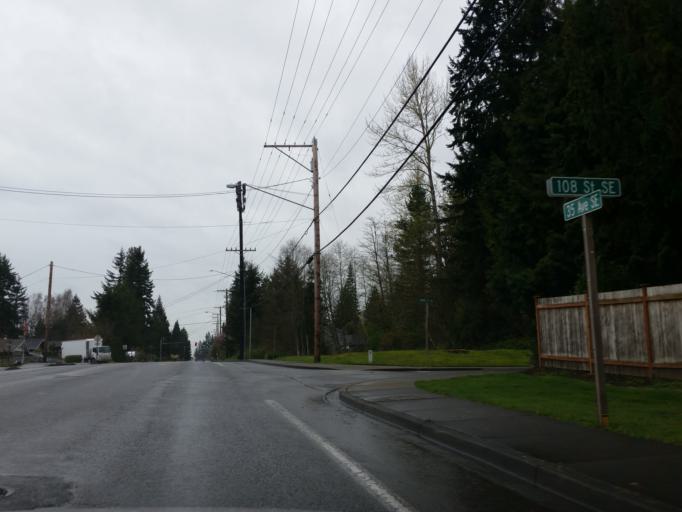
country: US
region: Washington
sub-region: Snohomish County
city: Mill Creek
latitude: 47.8997
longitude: -122.1854
